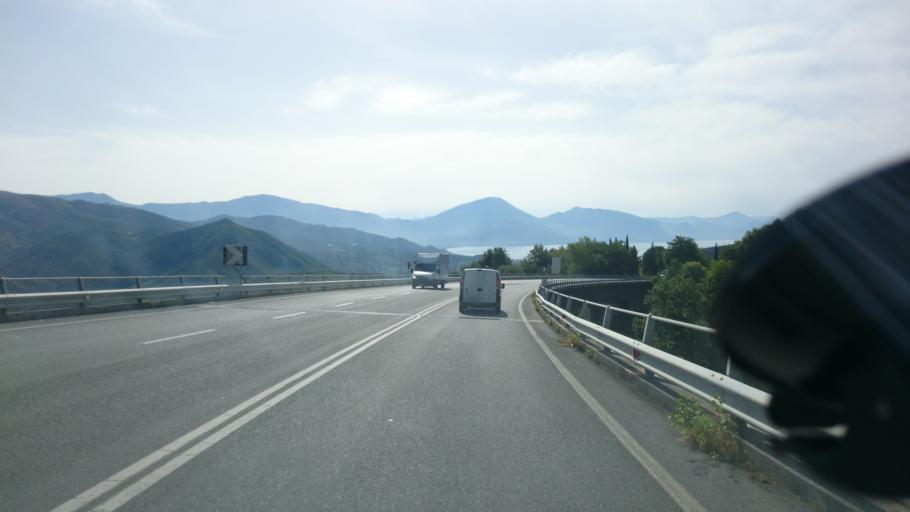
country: IT
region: Campania
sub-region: Provincia di Salerno
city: Scario
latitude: 40.0855
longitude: 15.4678
